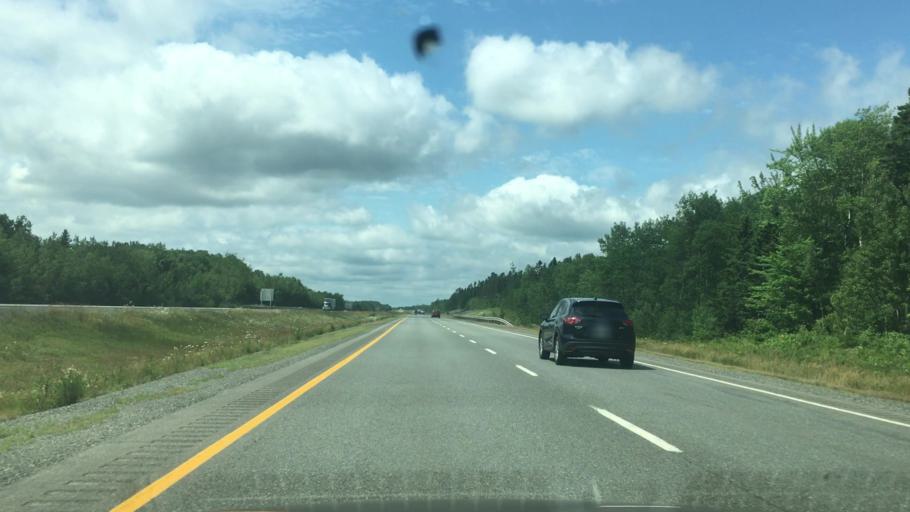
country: CA
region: Nova Scotia
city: Oxford
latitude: 45.7165
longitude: -63.9207
